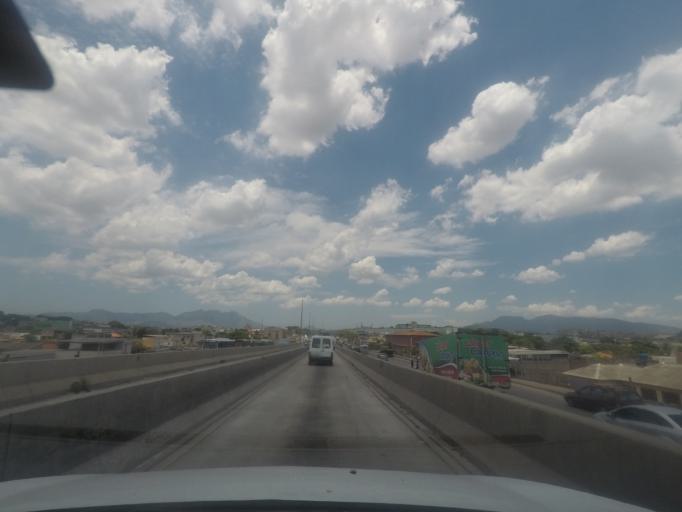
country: BR
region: Rio de Janeiro
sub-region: Sao Joao De Meriti
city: Sao Joao de Meriti
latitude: -22.8294
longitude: -43.3467
